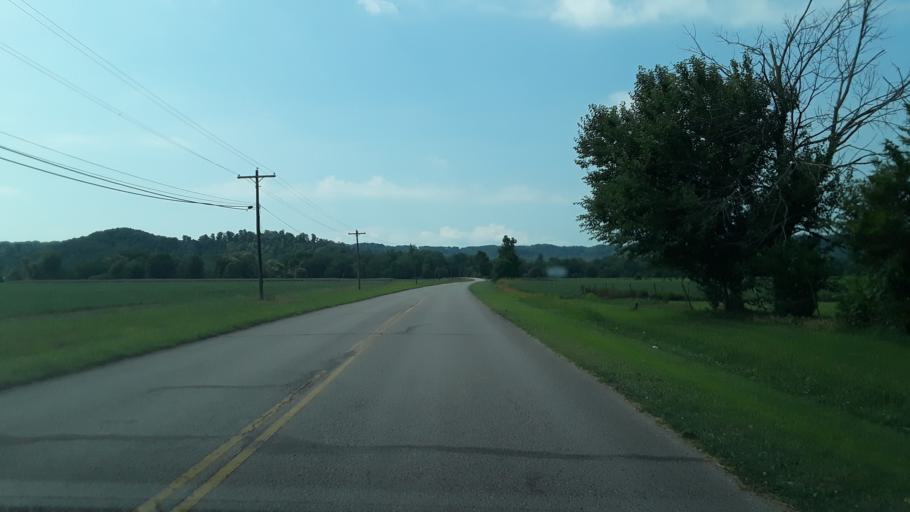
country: US
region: Indiana
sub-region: Clark County
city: Sellersburg
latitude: 38.4546
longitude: -85.8653
